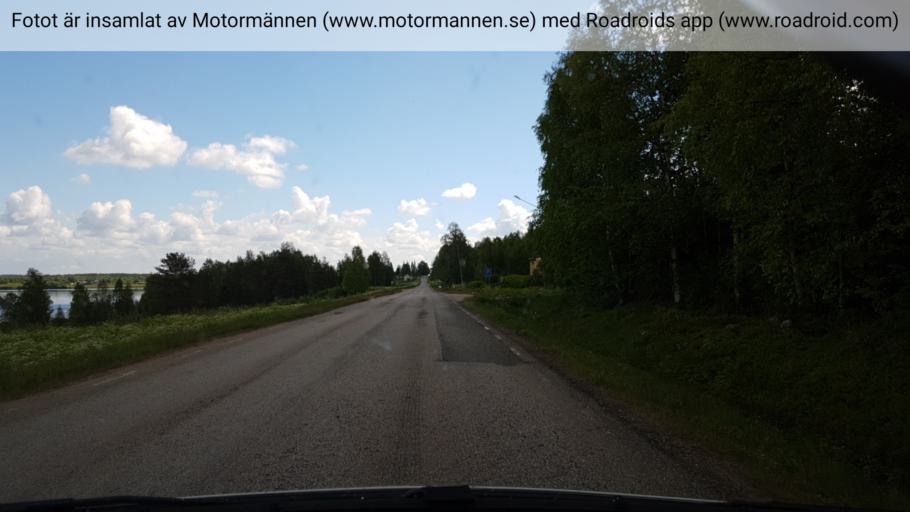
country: FI
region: Lapland
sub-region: Torniolaakso
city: Ylitornio
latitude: 66.1849
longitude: 23.7664
